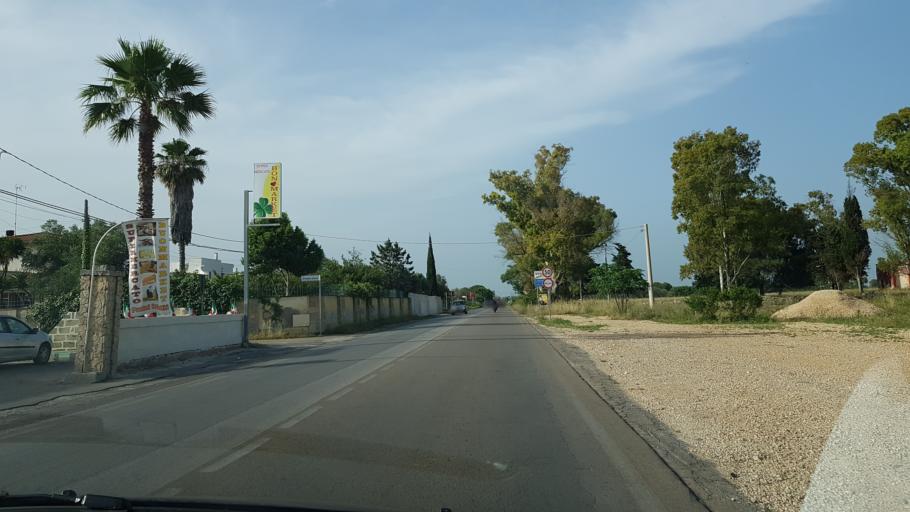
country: IT
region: Apulia
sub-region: Provincia di Lecce
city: Porto Cesareo
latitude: 40.2986
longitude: 17.8573
